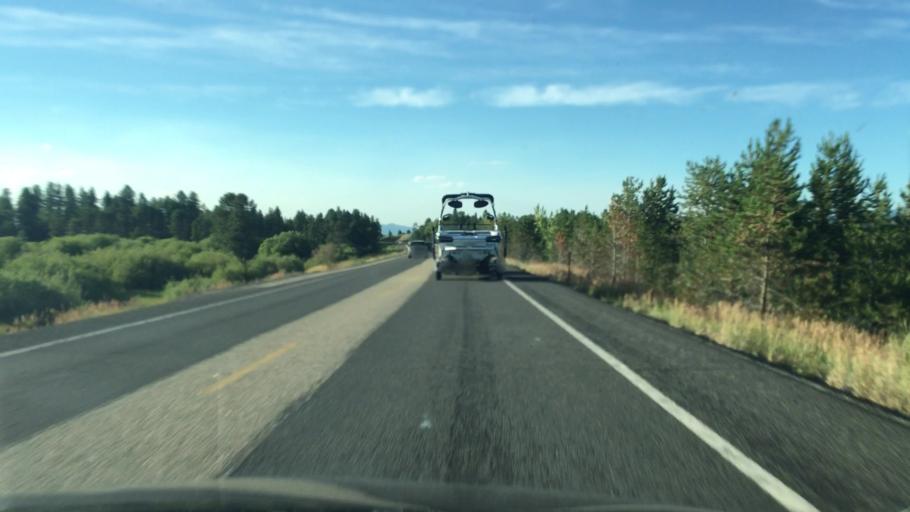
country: US
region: Idaho
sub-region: Valley County
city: Cascade
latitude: 44.6956
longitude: -116.0513
